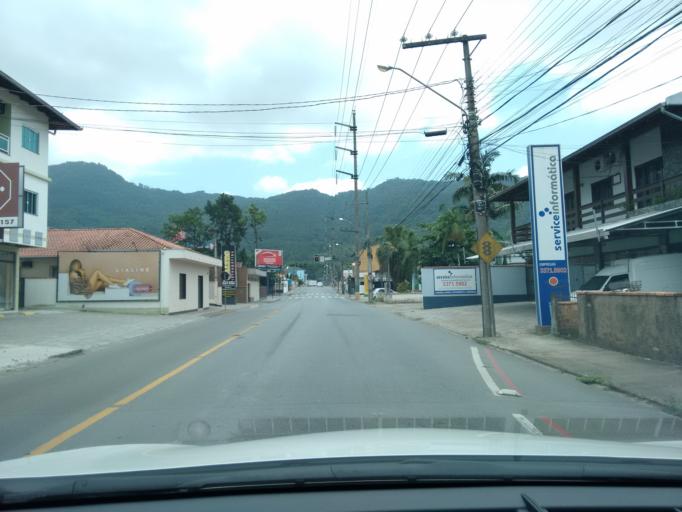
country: BR
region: Santa Catarina
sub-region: Jaragua Do Sul
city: Jaragua do Sul
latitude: -26.4844
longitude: -49.0567
